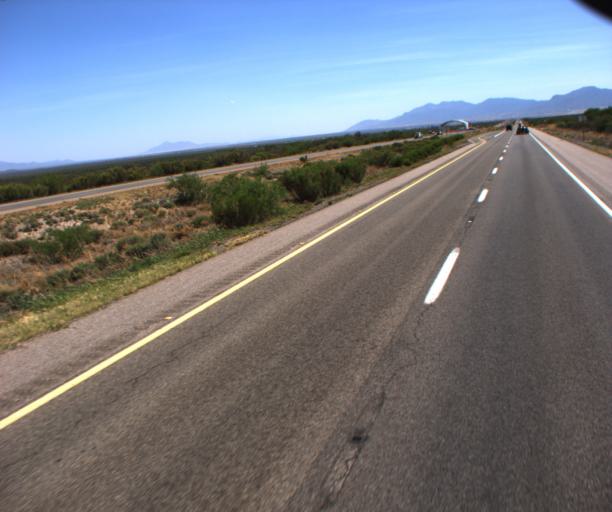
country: US
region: Arizona
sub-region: Cochise County
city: Huachuca City
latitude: 31.7548
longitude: -110.3503
